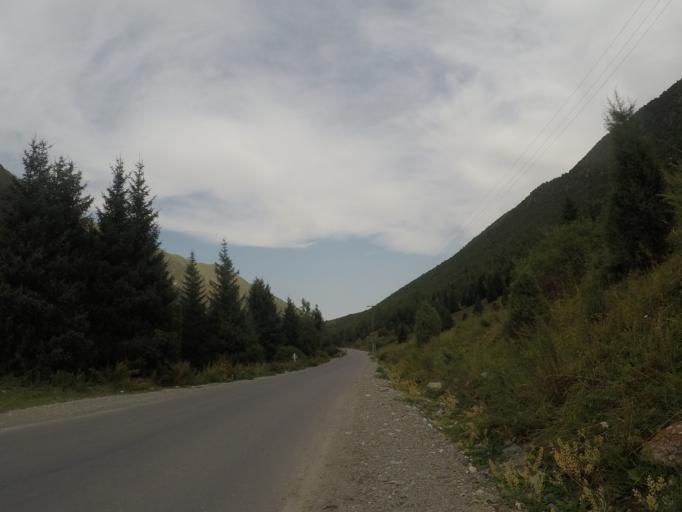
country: KG
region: Chuy
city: Bishkek
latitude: 42.5918
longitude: 74.4833
